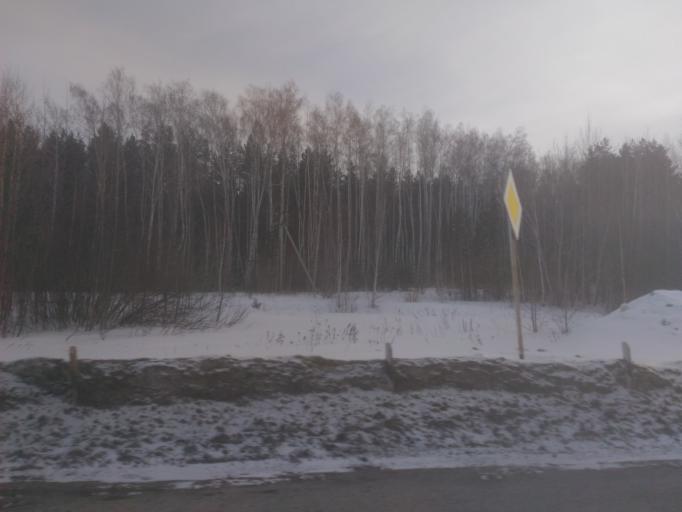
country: RU
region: Ulyanovsk
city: Isheyevka
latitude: 54.3756
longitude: 48.3096
